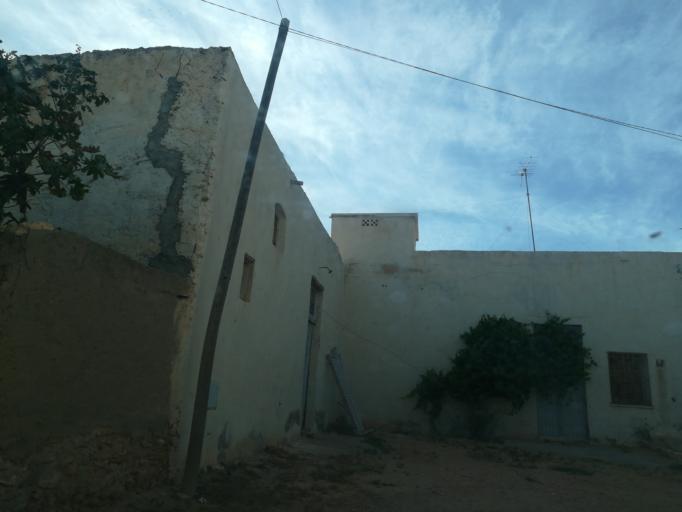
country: TN
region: Safaqis
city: Al Qarmadah
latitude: 34.8086
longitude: 10.7577
